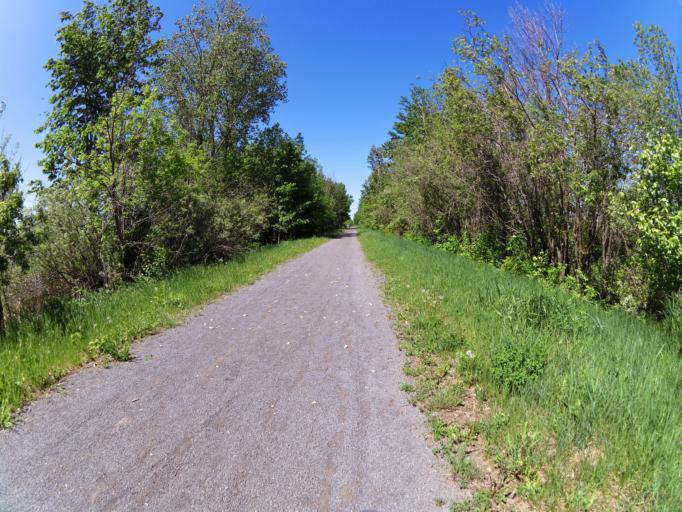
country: CA
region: Ontario
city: Clarence-Rockland
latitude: 45.4204
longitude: -75.3661
